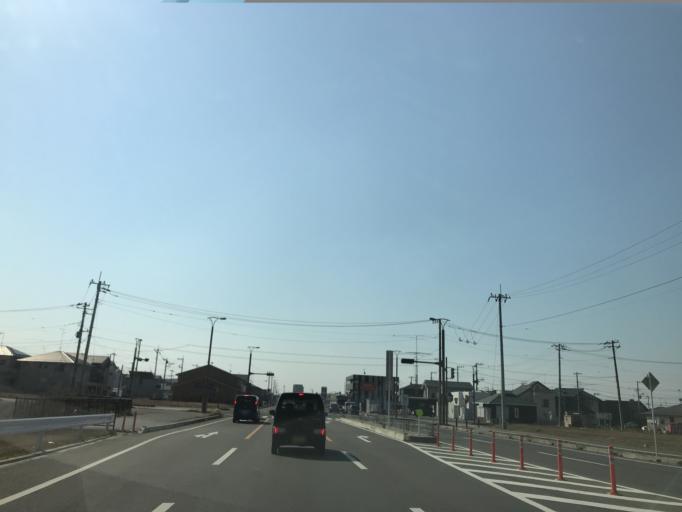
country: JP
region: Ibaraki
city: Mitsukaido
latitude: 36.0069
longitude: 140.0340
